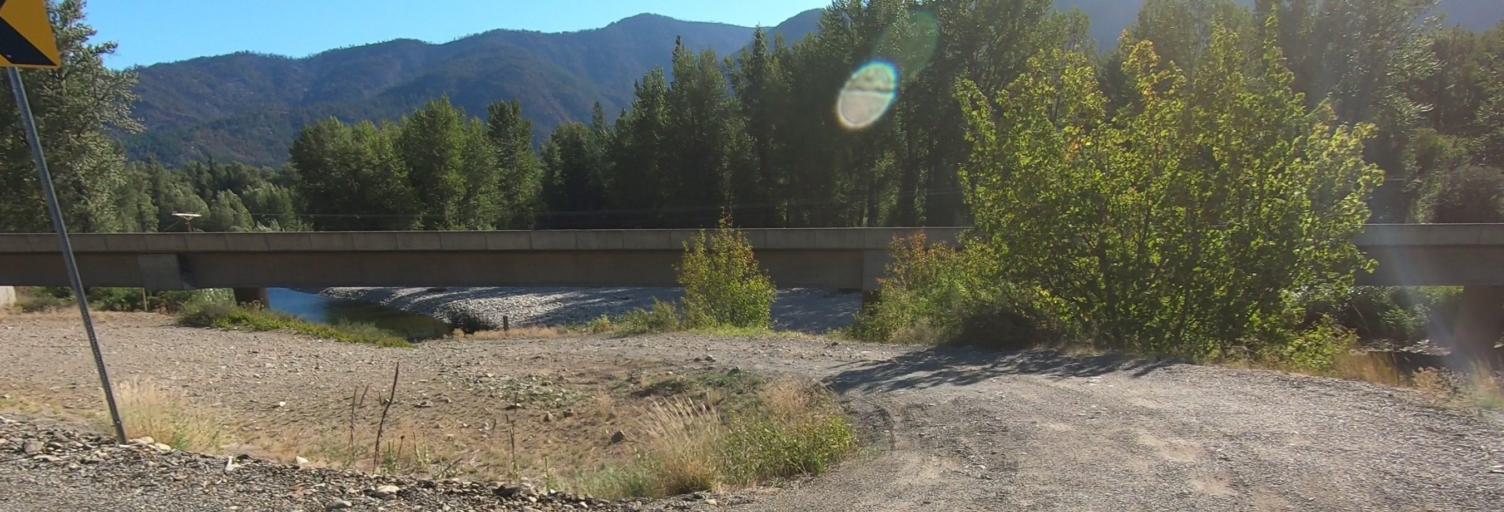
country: US
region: Washington
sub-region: Chelan County
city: Granite Falls
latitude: 48.5444
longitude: -120.3231
